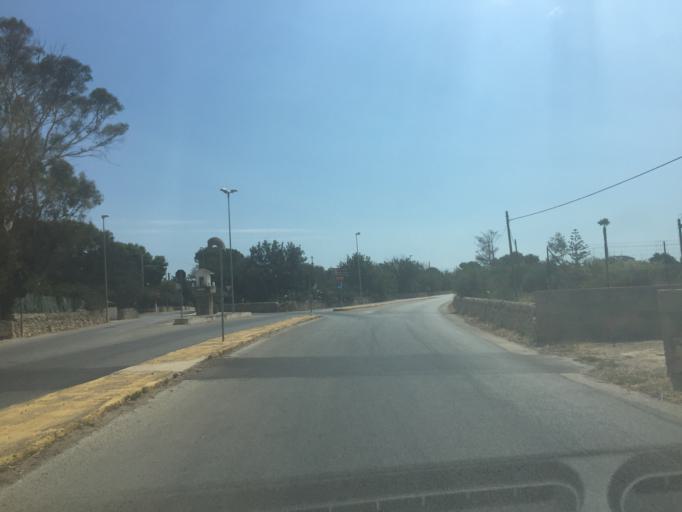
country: IT
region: Sicily
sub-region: Ragusa
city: Santa Croce Camerina
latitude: 36.8076
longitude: 14.5158
